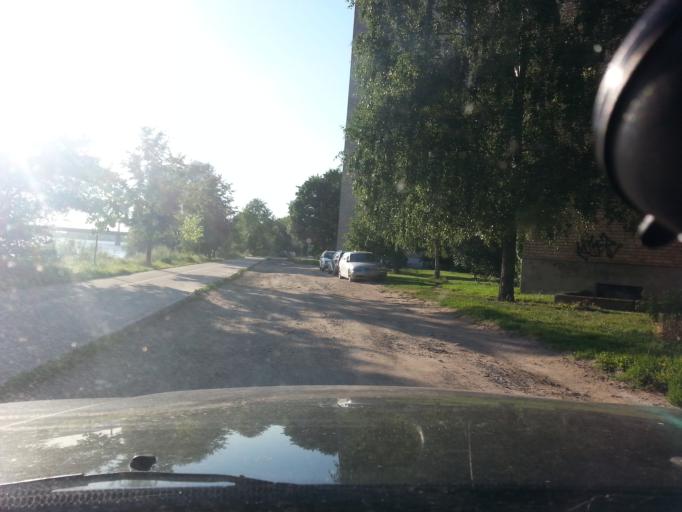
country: LV
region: Kekava
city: Balozi
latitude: 56.9143
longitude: 24.1680
